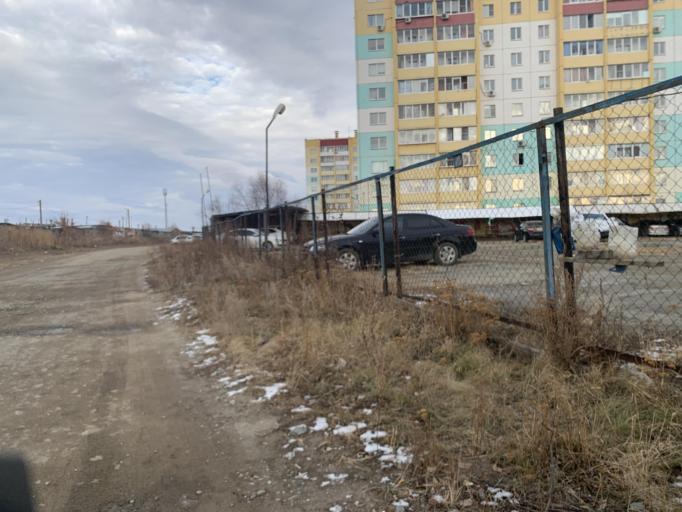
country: RU
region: Chelyabinsk
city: Roshchino
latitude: 55.1890
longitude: 61.2700
